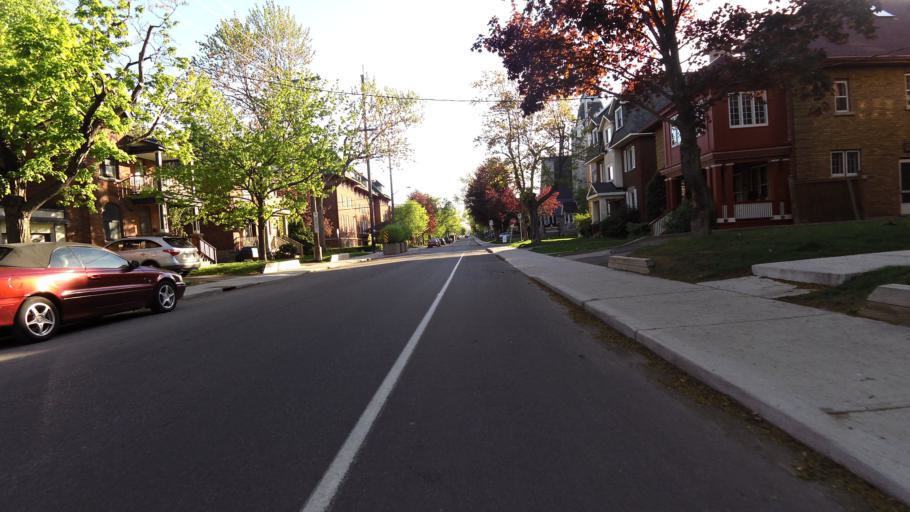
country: CA
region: Ontario
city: Ottawa
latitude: 45.4035
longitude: -75.6912
